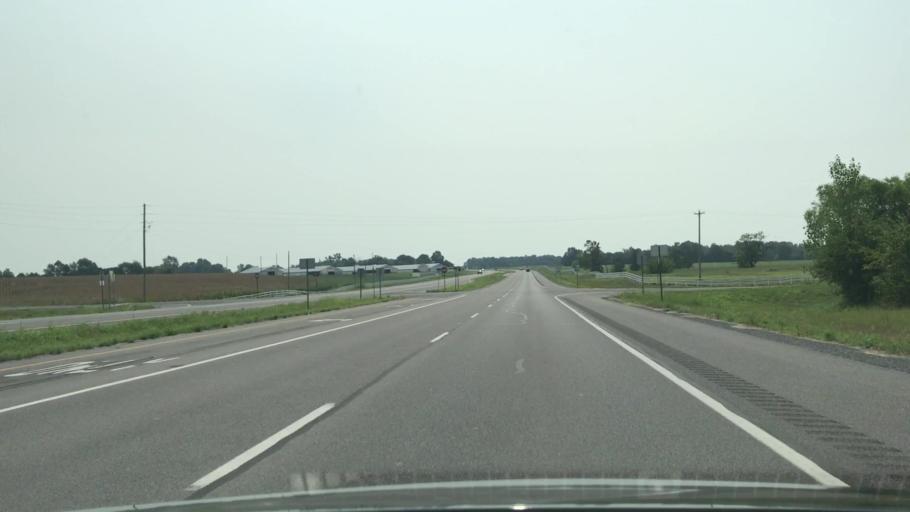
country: US
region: Kentucky
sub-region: Graves County
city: Mayfield
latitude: 36.6820
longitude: -88.5340
